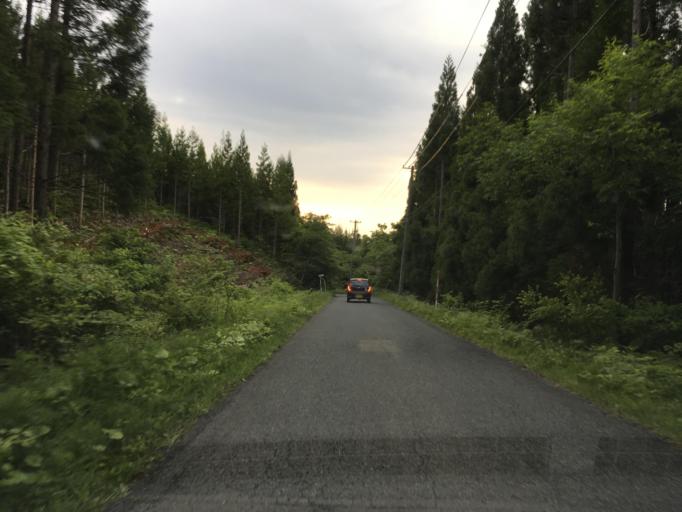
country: JP
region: Iwate
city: Mizusawa
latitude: 39.1480
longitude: 141.3019
